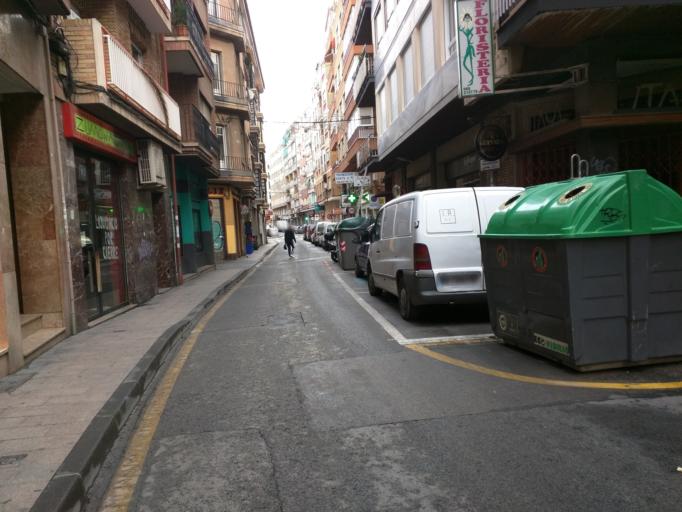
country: ES
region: Murcia
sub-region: Murcia
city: Murcia
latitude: 37.9856
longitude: -1.1248
